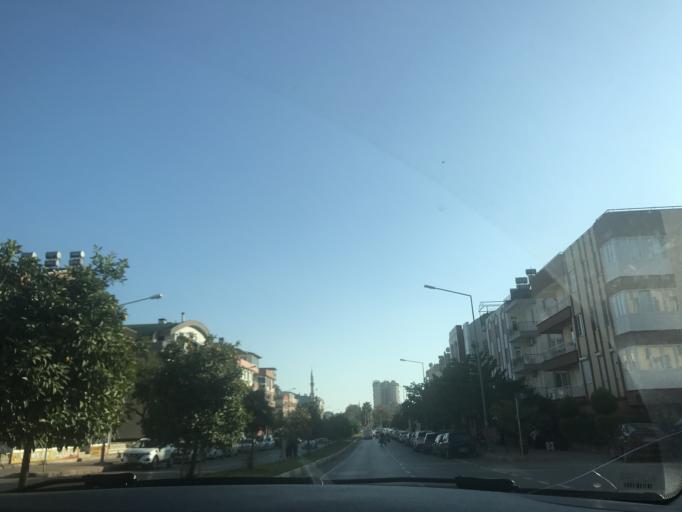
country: TR
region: Antalya
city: Antalya
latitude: 36.8853
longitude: 30.6477
